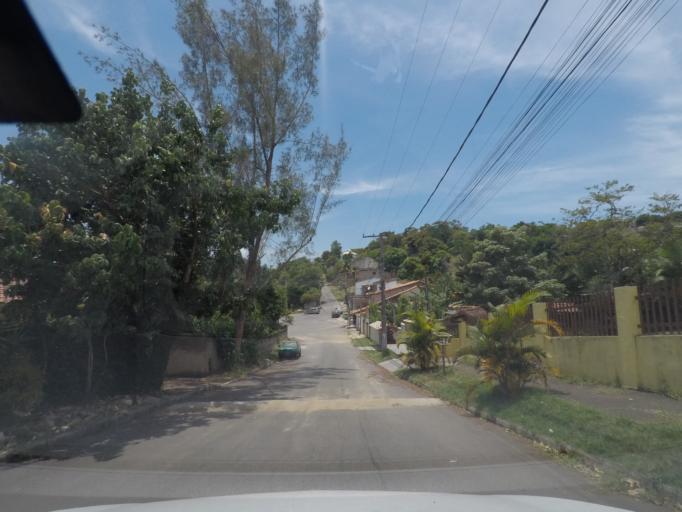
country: BR
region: Rio de Janeiro
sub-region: Marica
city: Marica
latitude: -22.9247
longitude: -42.8252
